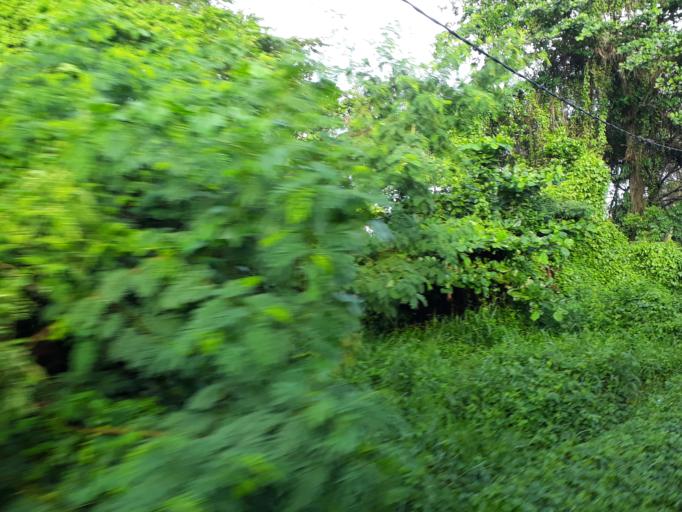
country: LK
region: Western
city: Kalutara
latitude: 6.5812
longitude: 79.9601
